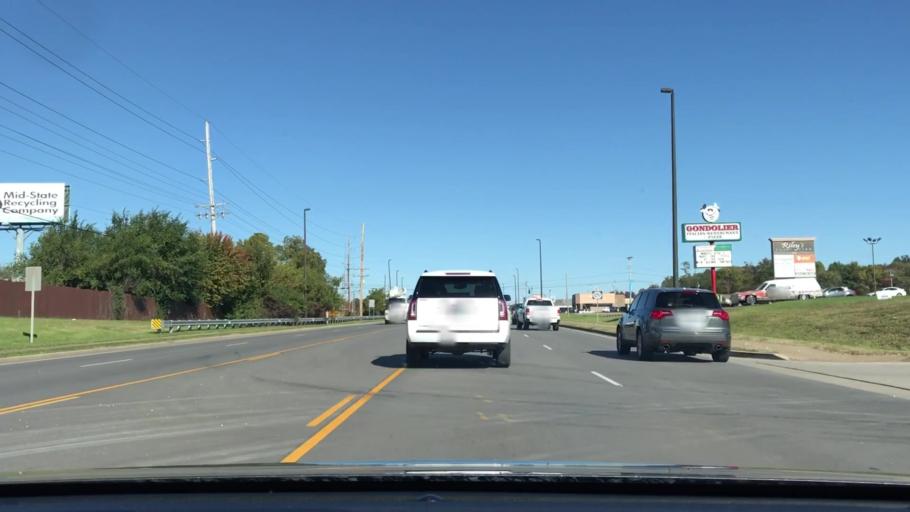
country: US
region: Kentucky
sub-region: Barren County
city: Glasgow
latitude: 36.9872
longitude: -85.9319
